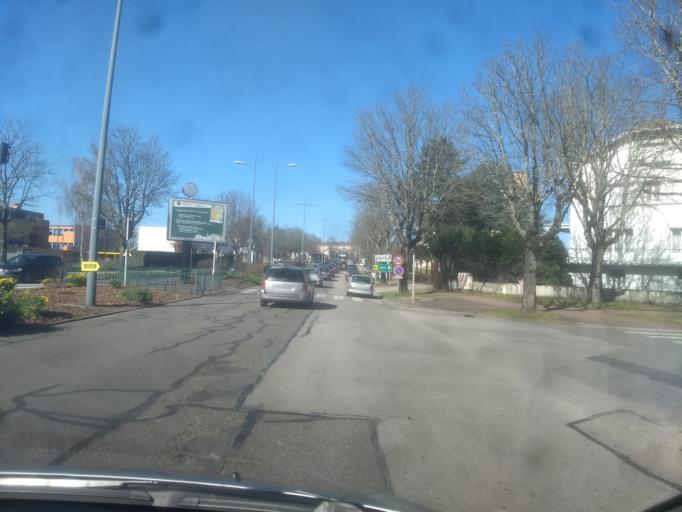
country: FR
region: Limousin
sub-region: Departement de la Haute-Vienne
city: Isle
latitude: 45.8224
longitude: 1.2283
